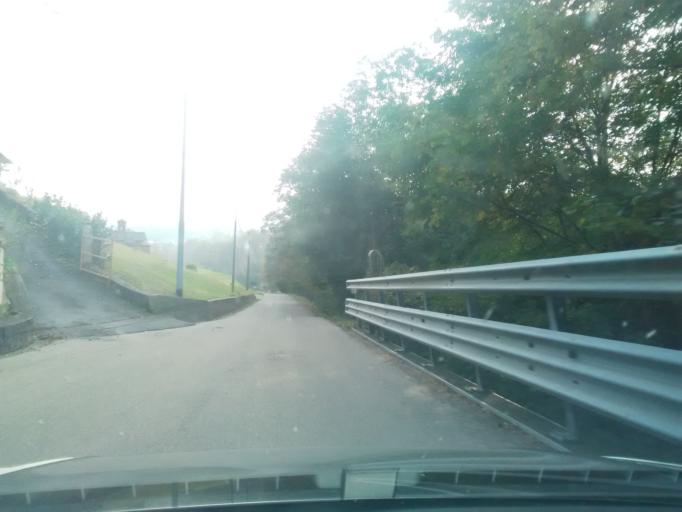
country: IT
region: Piedmont
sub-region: Provincia di Biella
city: Zumaglia
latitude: 45.5999
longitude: 8.0797
